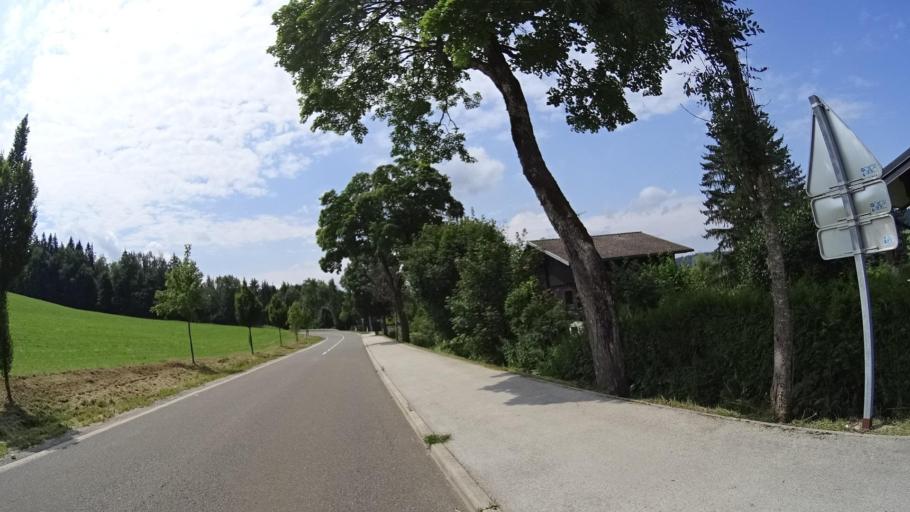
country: FR
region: Franche-Comte
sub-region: Departement du Doubs
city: Les Fourgs
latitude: 46.8153
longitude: 6.3233
